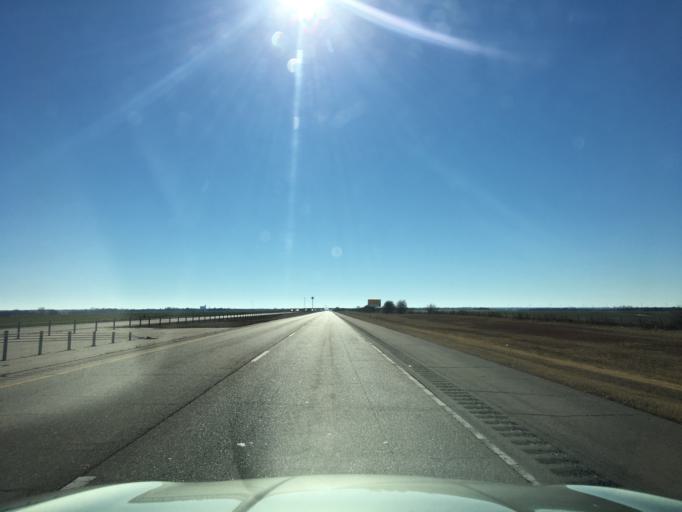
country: US
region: Oklahoma
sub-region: Kay County
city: Blackwell
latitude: 36.9672
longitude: -97.3458
